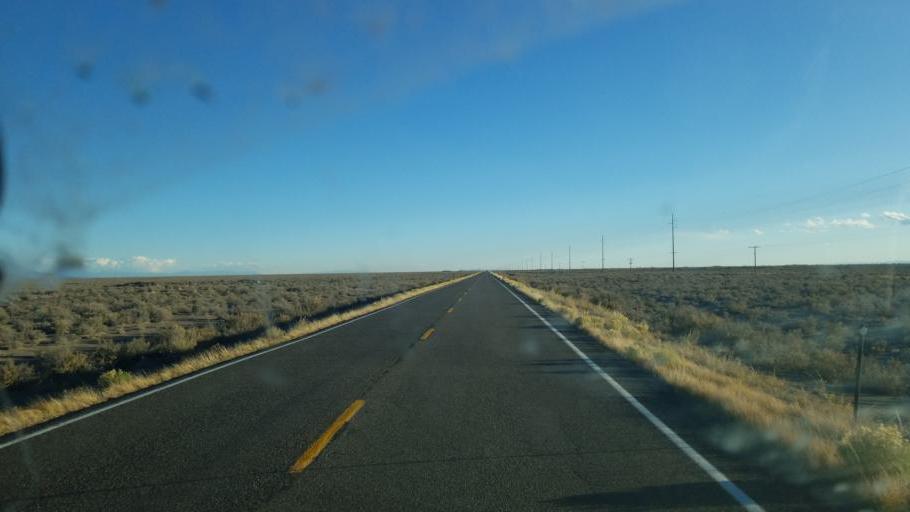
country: US
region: Colorado
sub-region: Saguache County
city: Center
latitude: 37.9091
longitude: -105.8984
